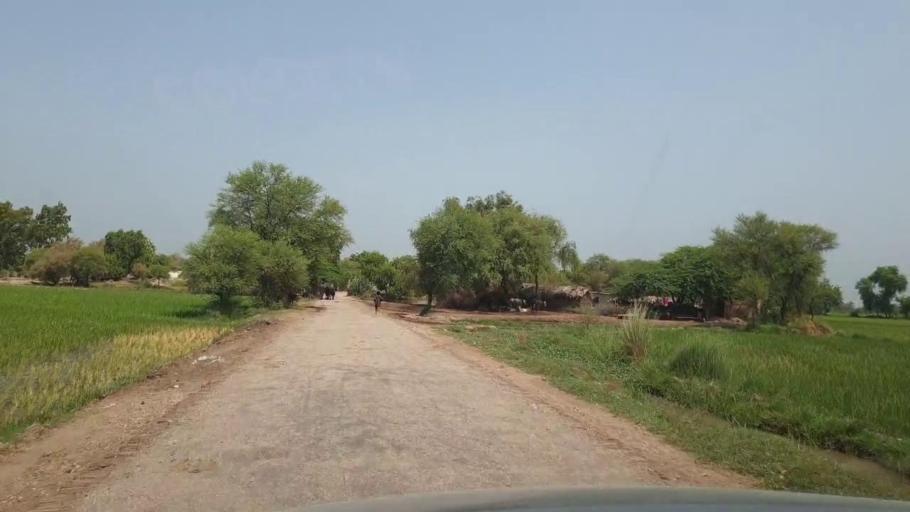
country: PK
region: Sindh
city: Madeji
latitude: 27.8072
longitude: 68.5204
